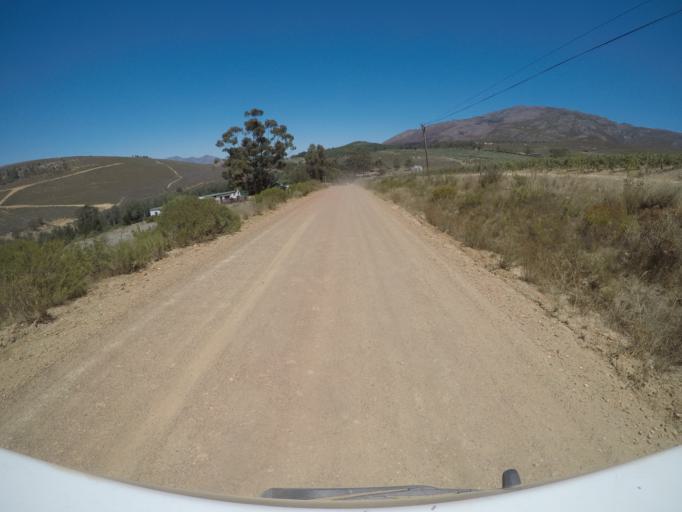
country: ZA
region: Western Cape
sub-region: Overberg District Municipality
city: Caledon
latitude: -34.1778
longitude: 19.2253
